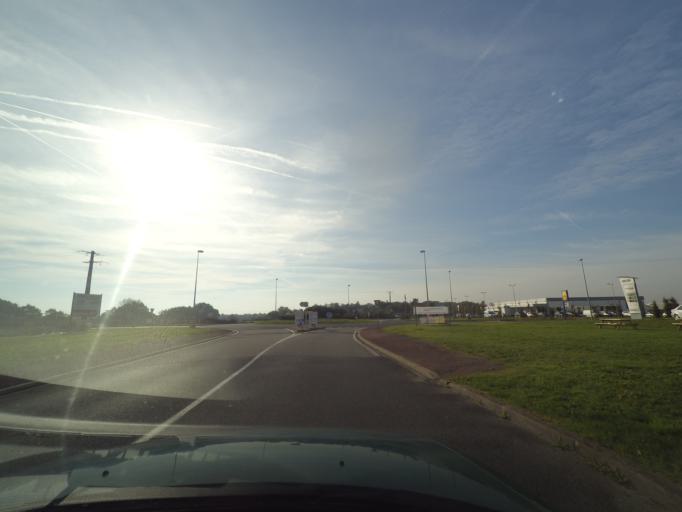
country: FR
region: Pays de la Loire
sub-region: Departement de la Vendee
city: Montaigu
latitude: 46.9801
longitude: -1.2985
